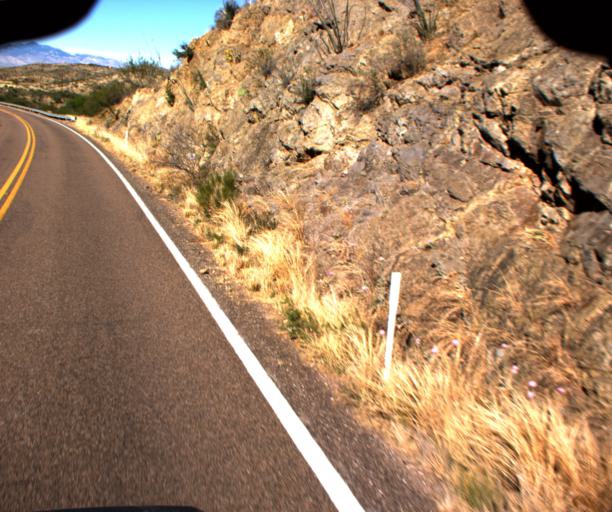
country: US
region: Arizona
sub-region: Pima County
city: Corona de Tucson
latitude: 31.8703
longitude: -110.6779
